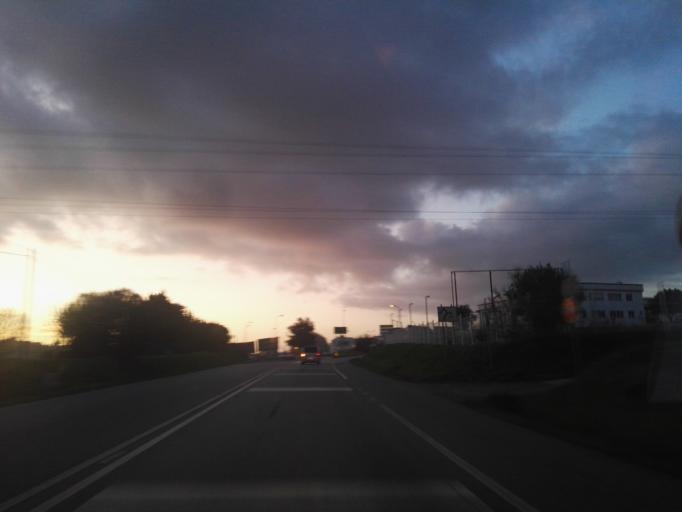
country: PT
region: Evora
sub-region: Montemor-O-Novo
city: Montemor-o-Novo
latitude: 38.6456
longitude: -8.1995
